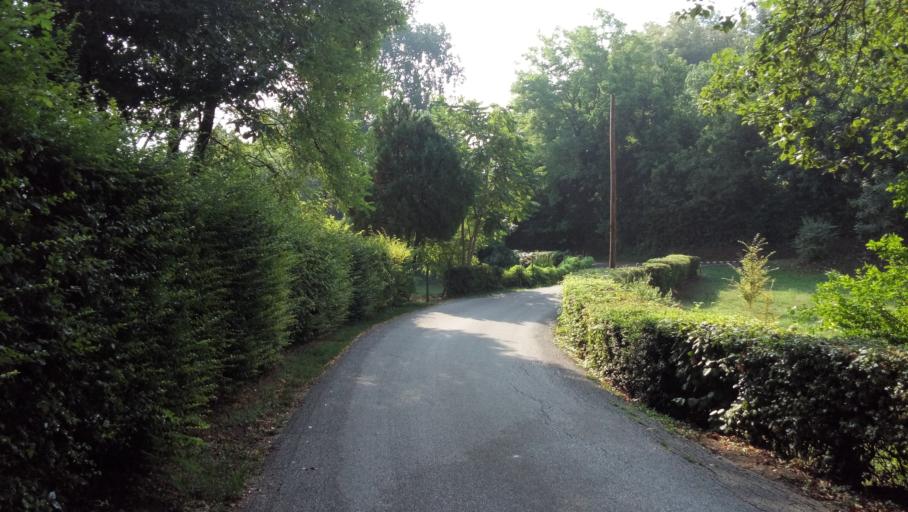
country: IT
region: Veneto
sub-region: Provincia di Vicenza
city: Sovizzo
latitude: 45.5396
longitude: 11.4596
